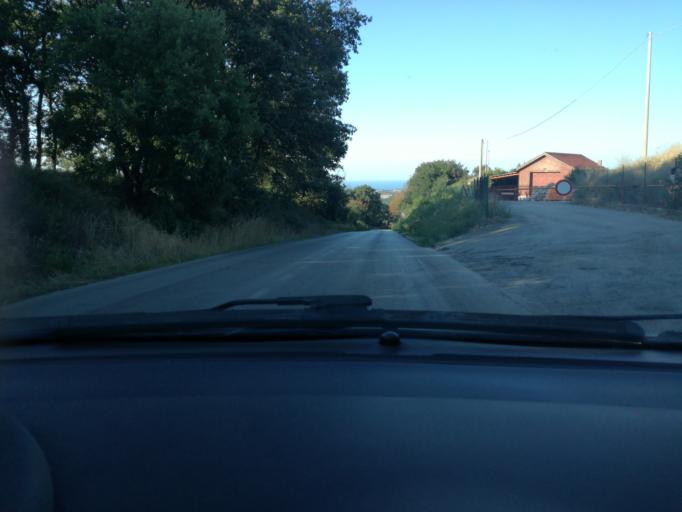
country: IT
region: Molise
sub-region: Provincia di Campobasso
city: Guglionesi
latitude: 41.9277
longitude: 14.9255
